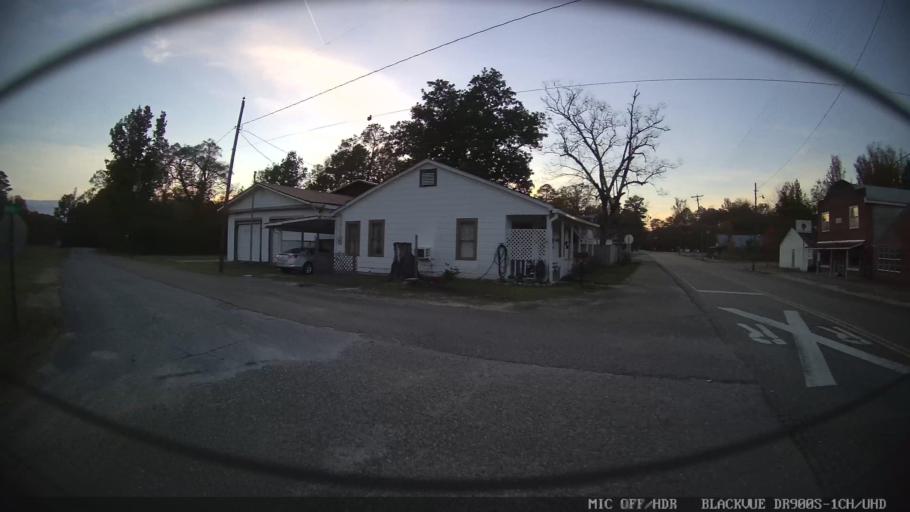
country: US
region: Mississippi
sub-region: Stone County
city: Wiggins
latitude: 31.0568
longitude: -89.1890
